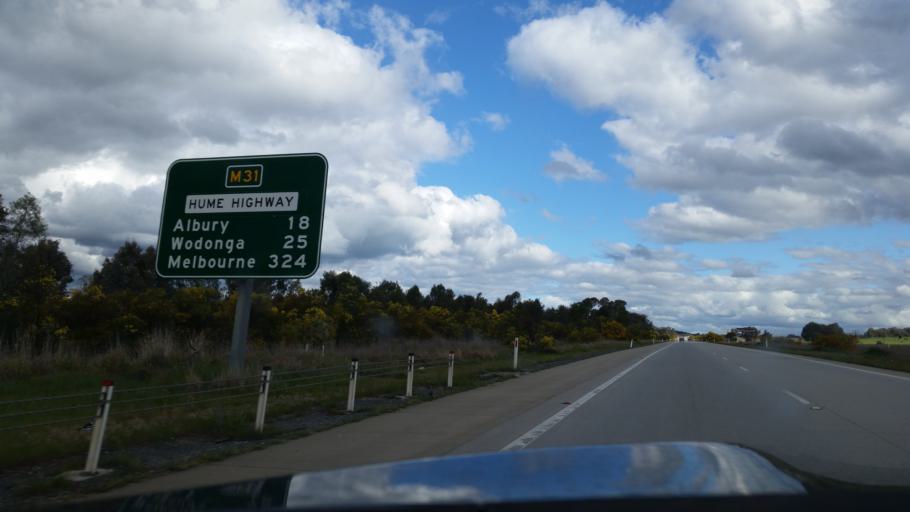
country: AU
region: New South Wales
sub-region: Greater Hume Shire
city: Jindera
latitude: -35.9413
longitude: 147.0035
